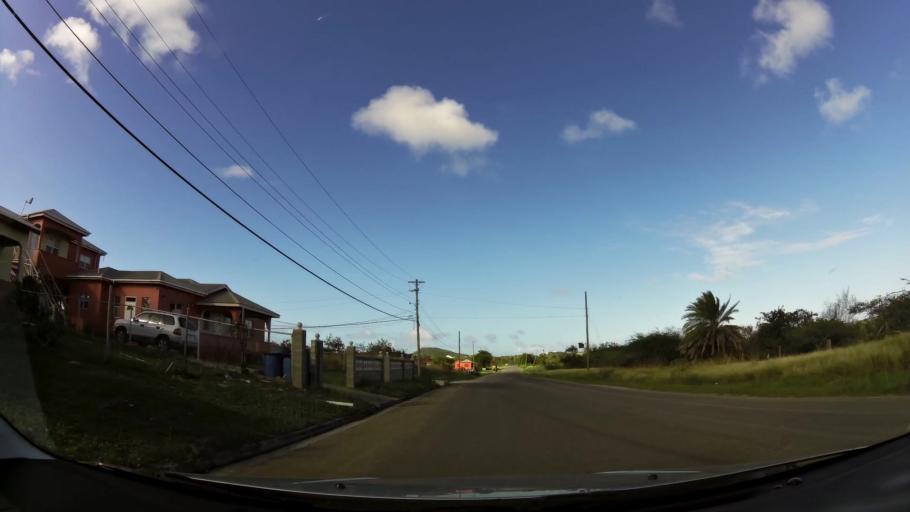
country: AG
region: Saint George
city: Piggotts
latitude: 17.1007
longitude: -61.8010
